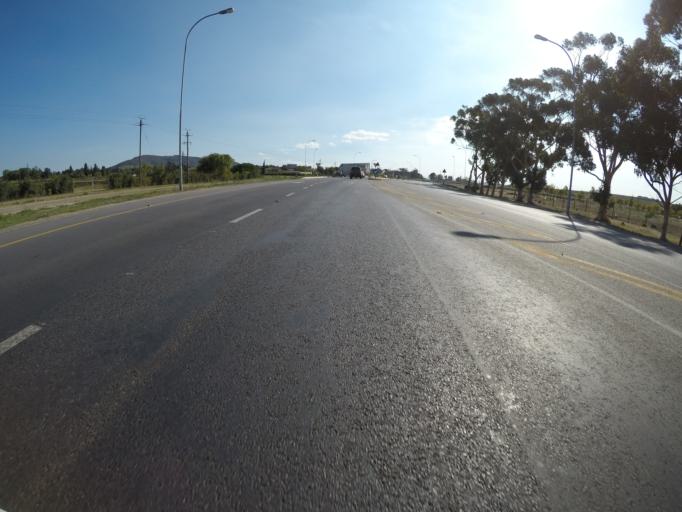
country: ZA
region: Western Cape
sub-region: Cape Winelands District Municipality
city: Stellenbosch
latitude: -33.8778
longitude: 18.8049
